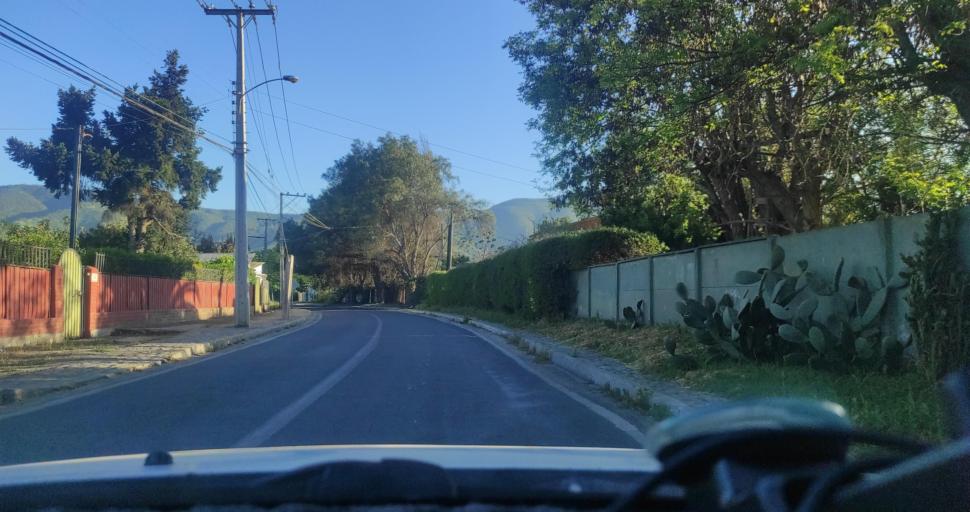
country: CL
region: Valparaiso
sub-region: Provincia de Marga Marga
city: Limache
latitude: -33.0046
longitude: -71.2237
